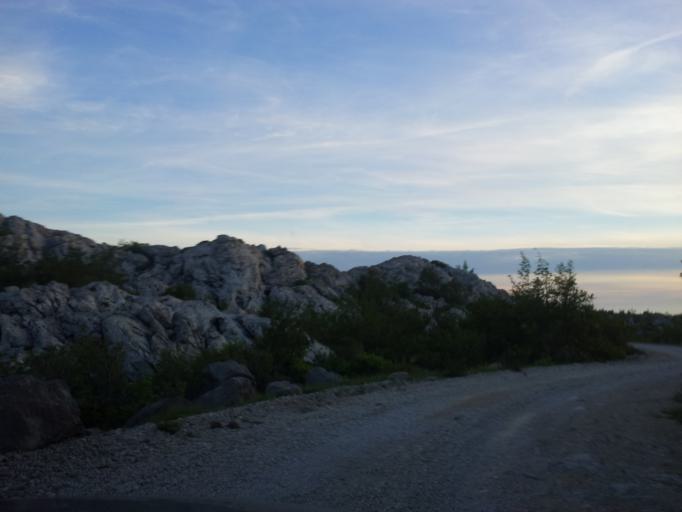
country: HR
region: Zadarska
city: Obrovac
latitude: 44.2602
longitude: 15.6408
